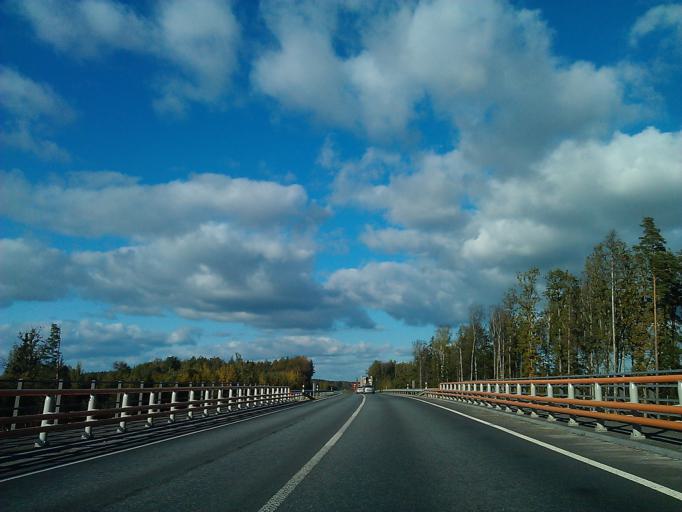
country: LV
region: Koknese
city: Koknese
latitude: 56.6476
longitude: 25.4555
